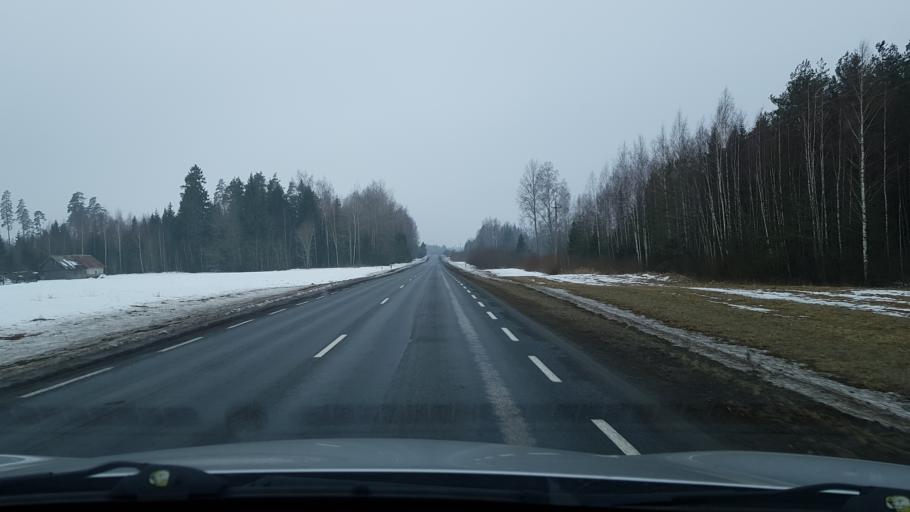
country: EE
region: Viljandimaa
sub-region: Viiratsi vald
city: Viiratsi
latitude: 58.2491
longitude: 25.7702
